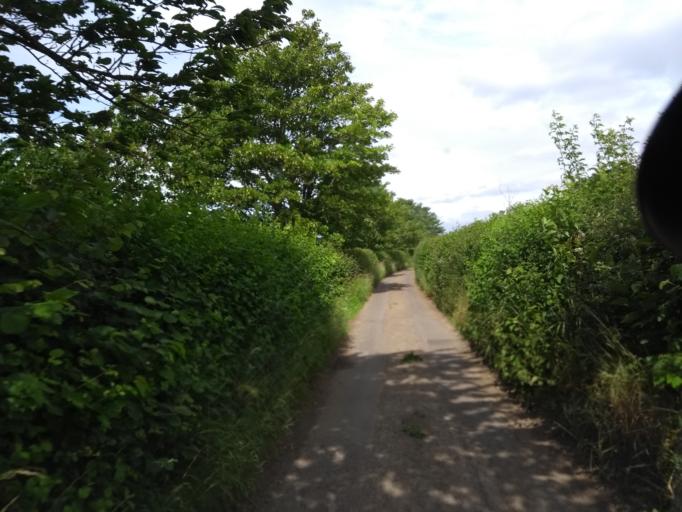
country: GB
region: England
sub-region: Somerset
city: Ilminster
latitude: 50.9246
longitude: -2.8658
